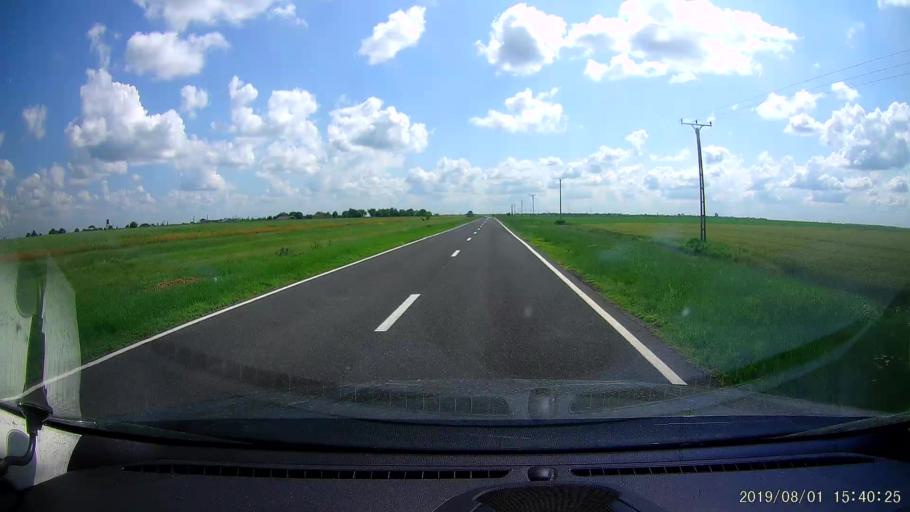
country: RO
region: Braila
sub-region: Comuna Baraganul
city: Baraganul
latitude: 44.8379
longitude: 27.5430
